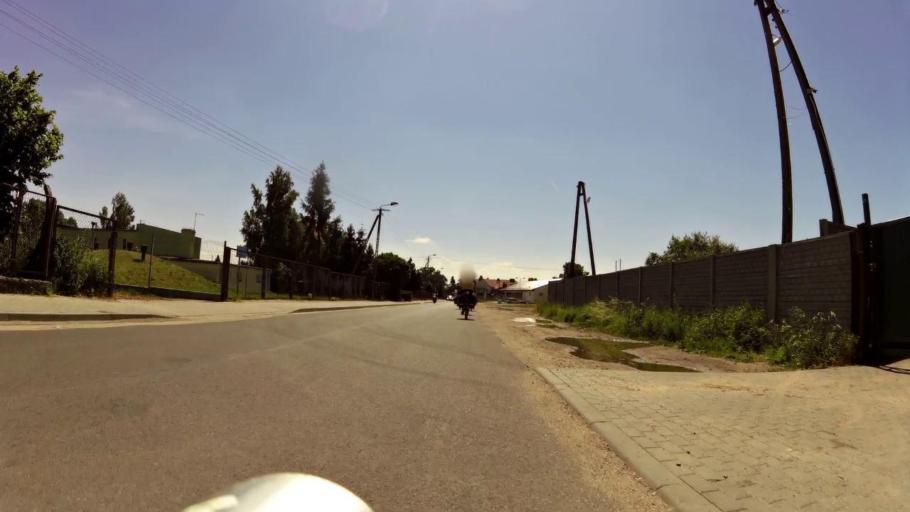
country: PL
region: Kujawsko-Pomorskie
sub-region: Powiat nakielski
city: Slesin
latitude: 53.1664
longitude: 17.7039
